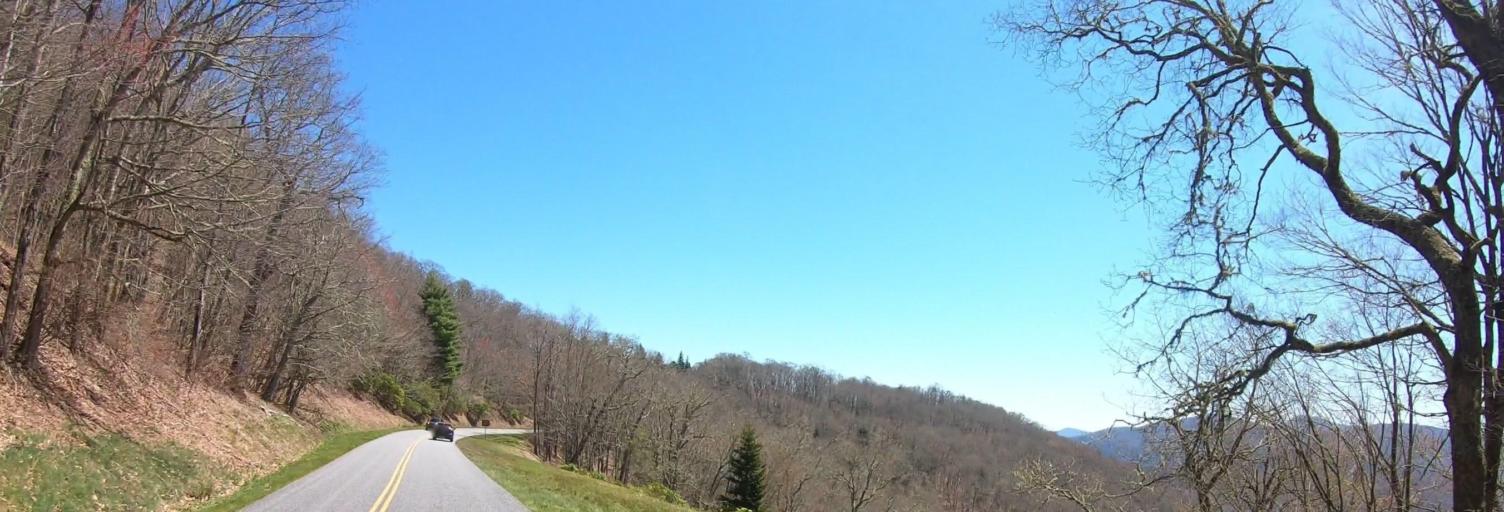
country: US
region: North Carolina
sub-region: Haywood County
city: Maggie Valley
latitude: 35.5096
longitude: -83.1826
